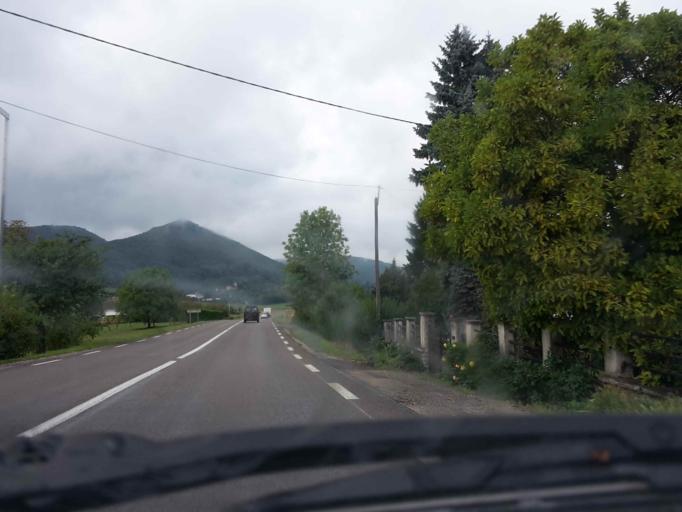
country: FR
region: Franche-Comte
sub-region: Departement du Doubs
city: Roulans
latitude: 47.3216
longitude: 6.2544
